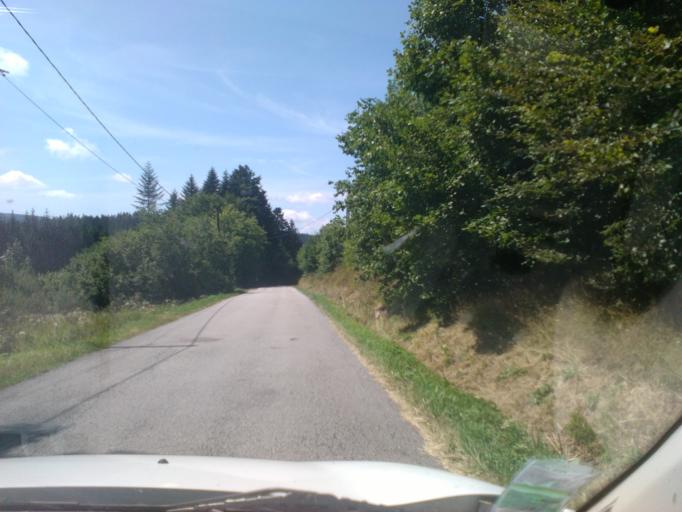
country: FR
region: Lorraine
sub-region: Departement des Vosges
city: La Bresse
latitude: 48.0409
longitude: 6.8315
